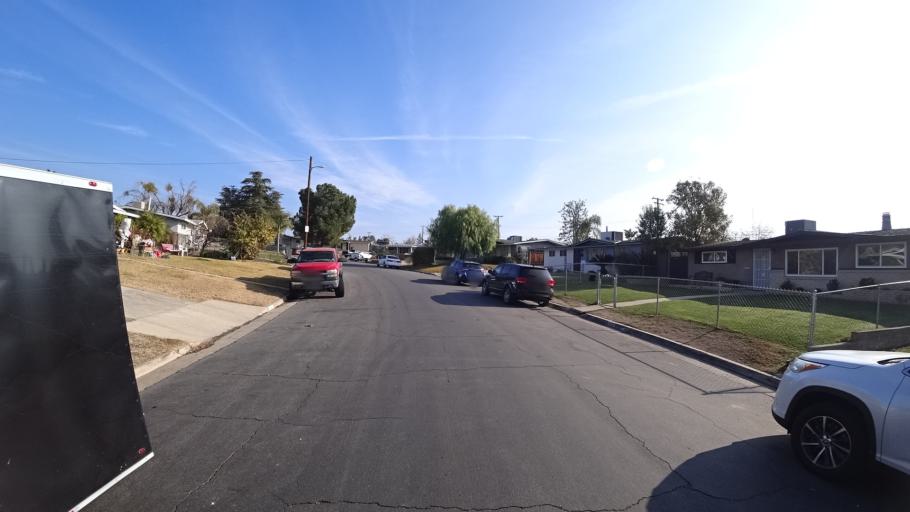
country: US
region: California
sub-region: Kern County
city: Oildale
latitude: 35.4045
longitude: -118.9804
